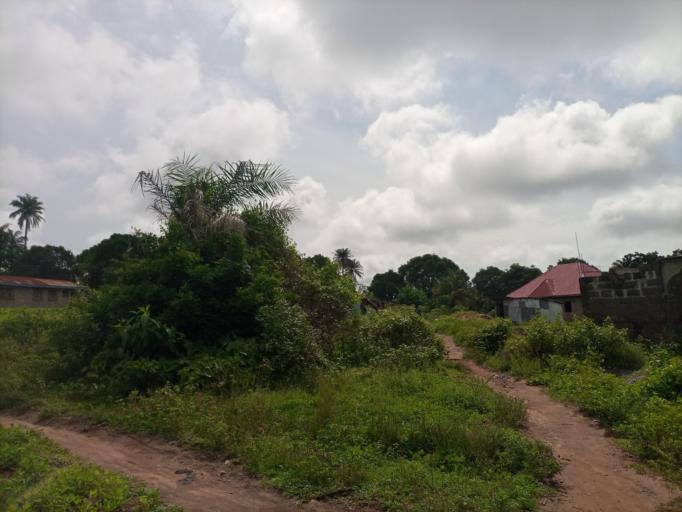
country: SL
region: Northern Province
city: Masoyila
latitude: 8.5973
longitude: -13.1747
